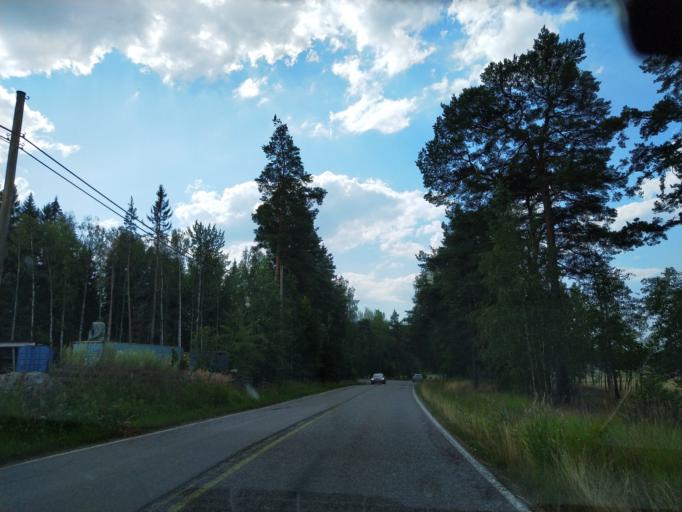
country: FI
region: Uusimaa
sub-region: Helsinki
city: Kirkkonummi
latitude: 60.0598
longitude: 24.4954
